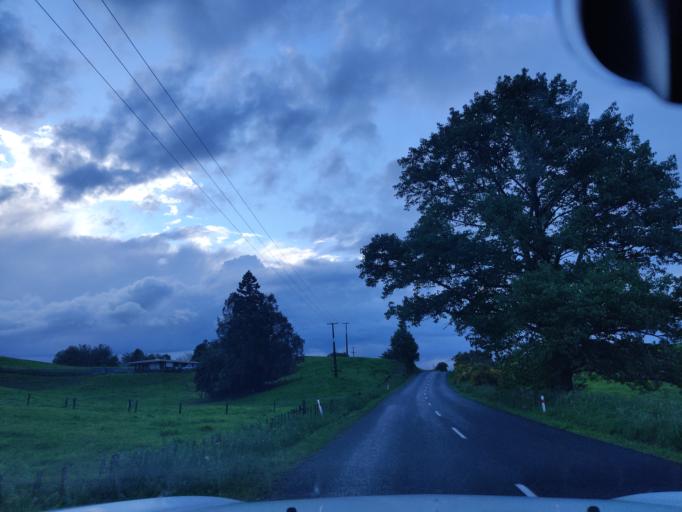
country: NZ
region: Waikato
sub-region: South Waikato District
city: Tokoroa
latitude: -38.2152
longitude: 175.8288
